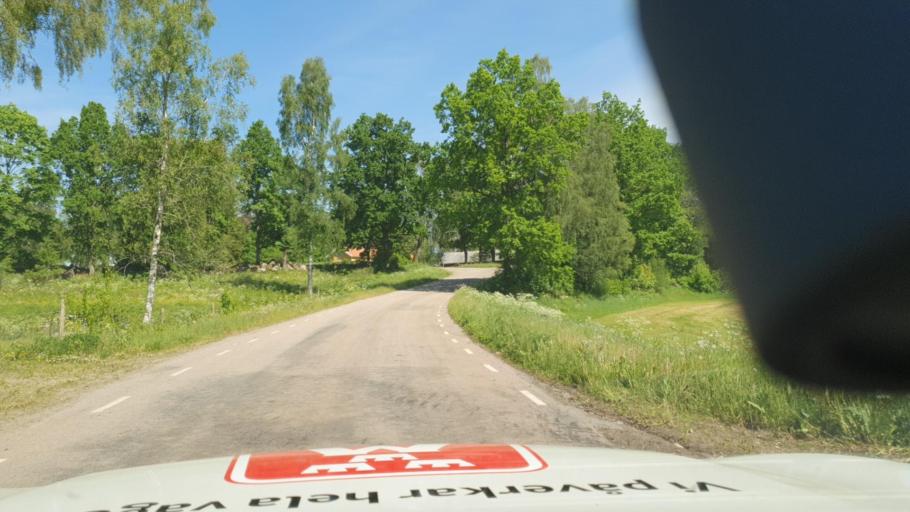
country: SE
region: Vaestra Goetaland
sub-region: Herrljunga Kommun
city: Herrljunga
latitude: 58.0010
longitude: 13.0871
